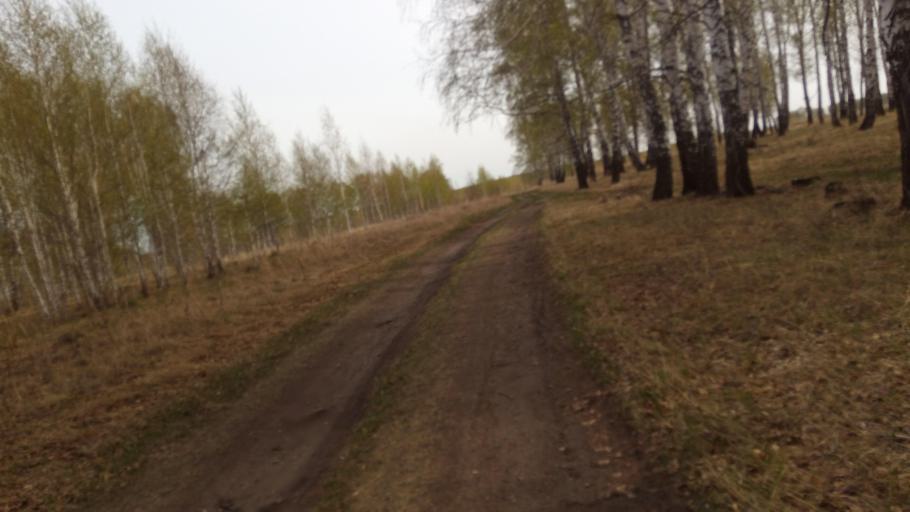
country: RU
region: Chelyabinsk
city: Timiryazevskiy
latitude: 55.0060
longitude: 60.8597
